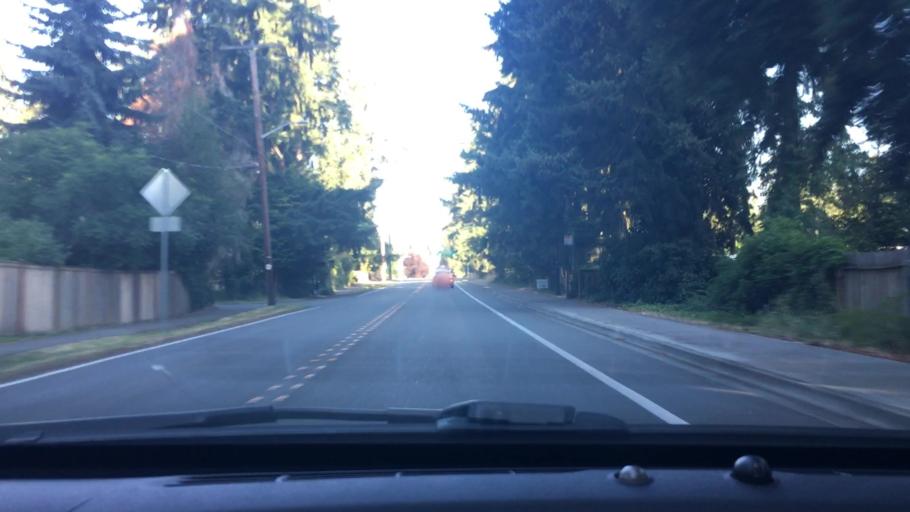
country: US
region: Washington
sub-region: King County
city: Sammamish
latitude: 47.6237
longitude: -122.1194
